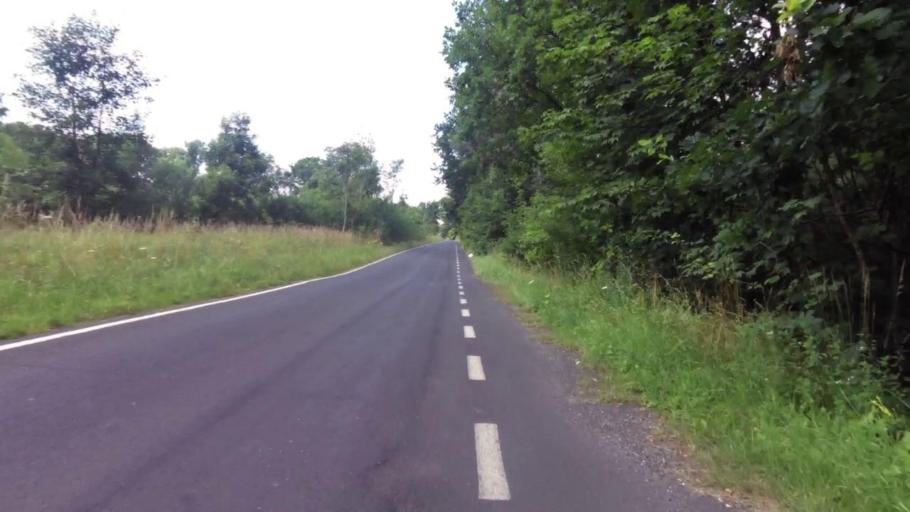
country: PL
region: West Pomeranian Voivodeship
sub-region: Powiat stargardzki
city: Insko
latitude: 53.4253
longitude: 15.4834
